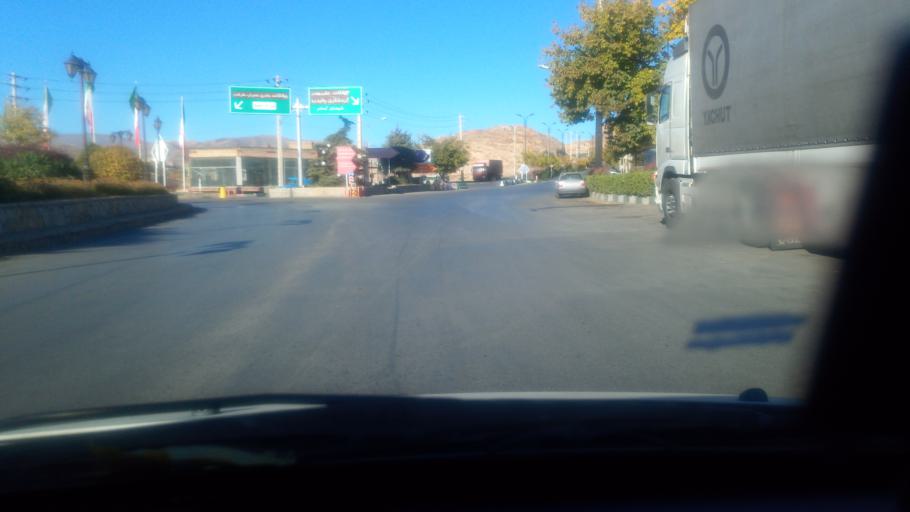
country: IR
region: Razavi Khorasan
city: Torqabeh
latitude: 36.3135
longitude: 59.3676
